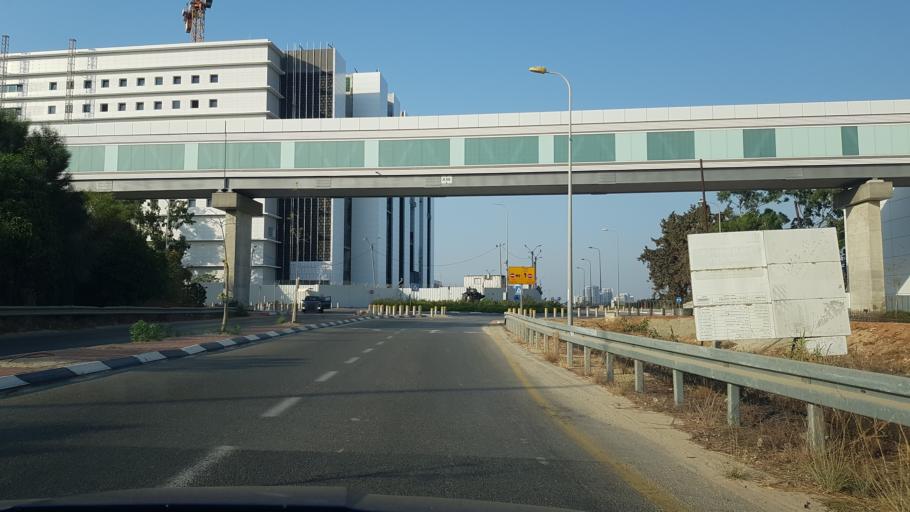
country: IL
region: Tel Aviv
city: Herzliyya
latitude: 32.1425
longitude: 34.8061
